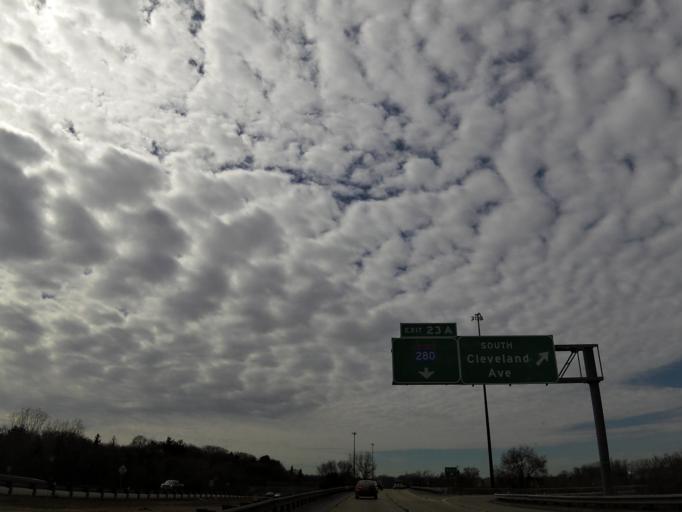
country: US
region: Minnesota
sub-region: Ramsey County
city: Lauderdale
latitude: 45.0103
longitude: -93.1869
